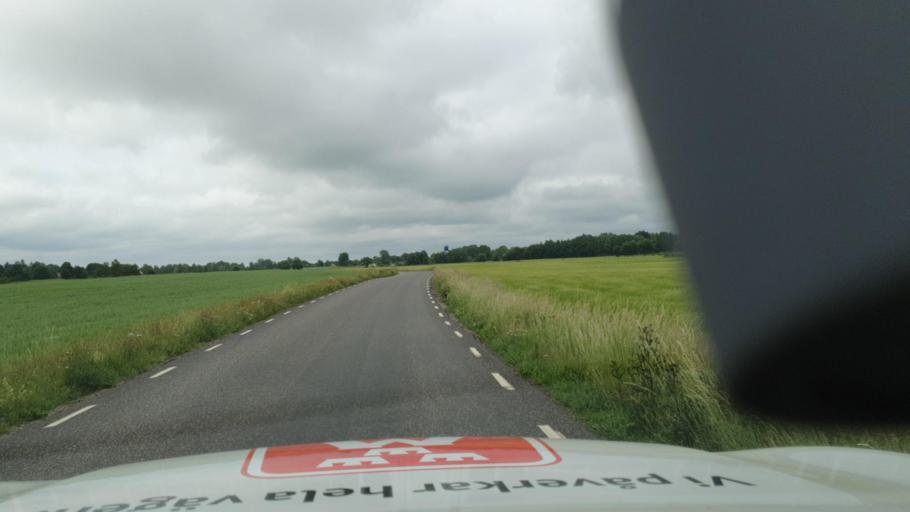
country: SE
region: Vaestra Goetaland
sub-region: Falkopings Kommun
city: Falkoeping
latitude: 58.0350
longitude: 13.5838
